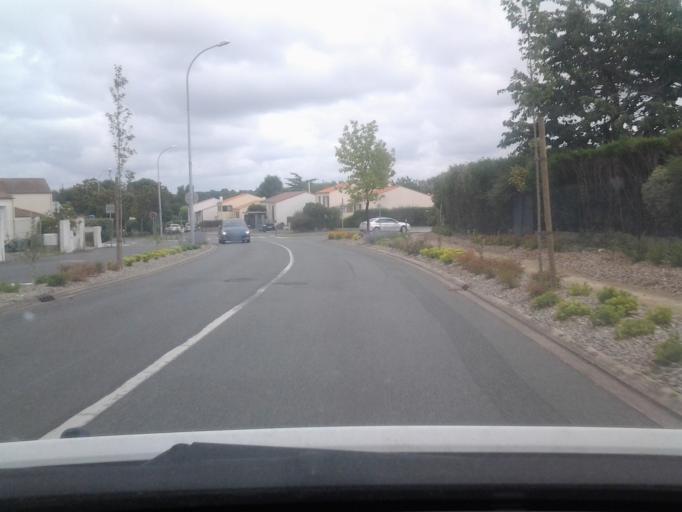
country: FR
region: Pays de la Loire
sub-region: Departement de la Vendee
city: La Roche-sur-Yon
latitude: 46.6509
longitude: -1.4300
